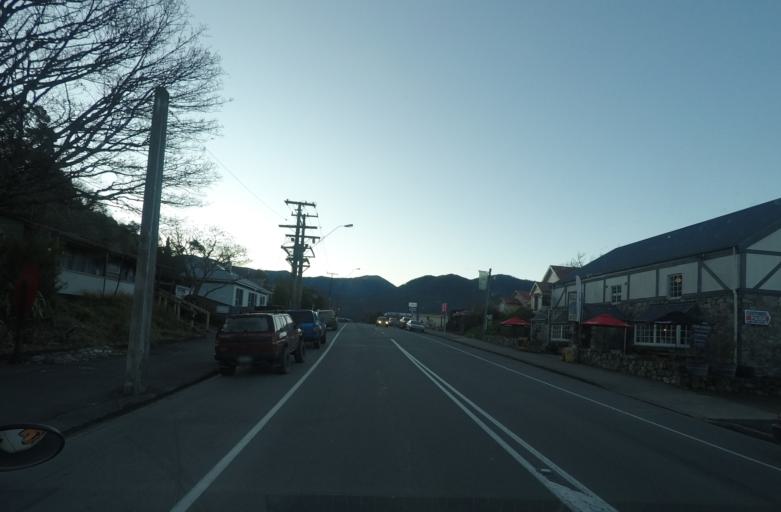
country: NZ
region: Marlborough
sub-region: Marlborough District
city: Picton
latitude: -41.2775
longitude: 173.7662
